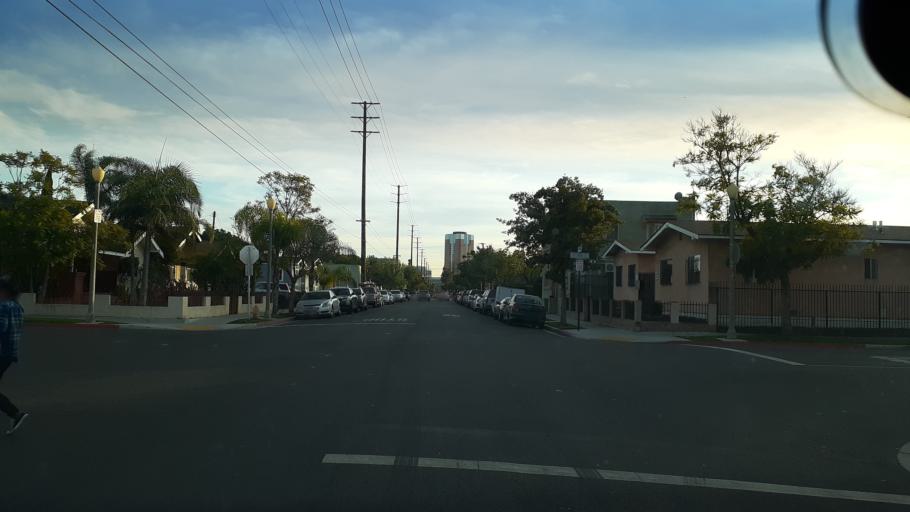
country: US
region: California
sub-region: Los Angeles County
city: Long Beach
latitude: 33.7804
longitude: -118.1994
